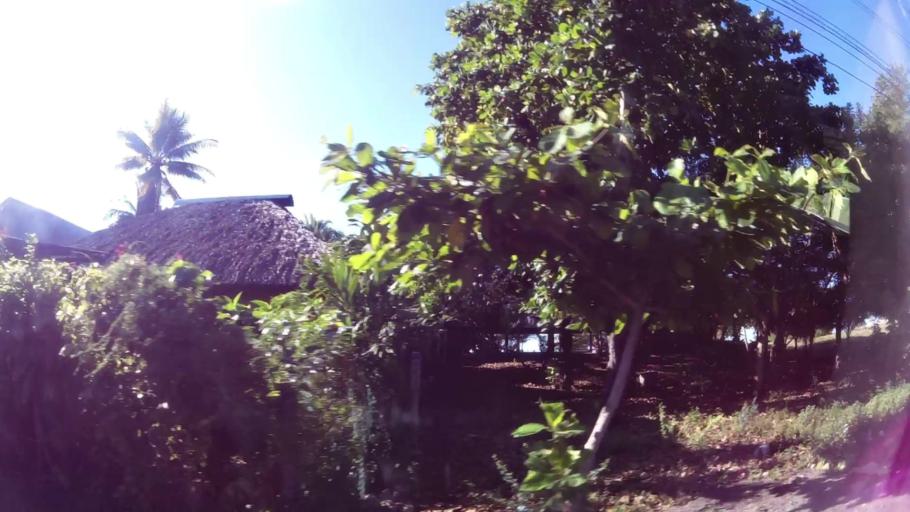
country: GT
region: Santa Rosa
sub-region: Municipio de Taxisco
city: Taxisco
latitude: 13.8898
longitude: -90.4806
